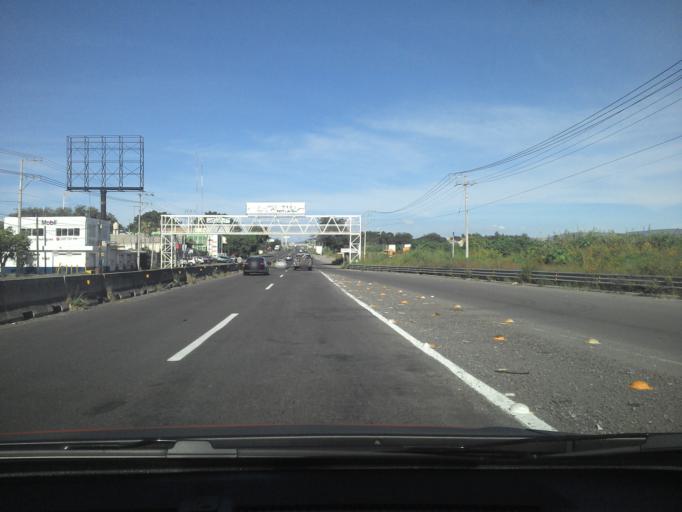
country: MX
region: Jalisco
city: El Refugio
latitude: 20.6663
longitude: -103.7200
